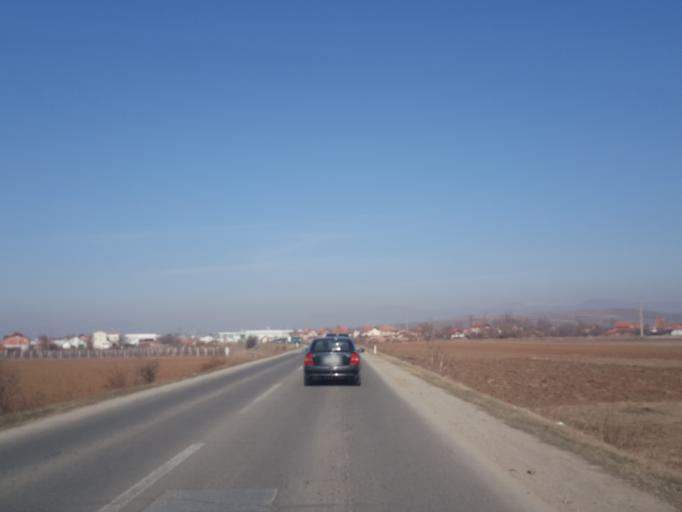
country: XK
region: Mitrovica
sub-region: Vushtrri
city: Vushtrri
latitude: 42.7788
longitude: 21.0140
